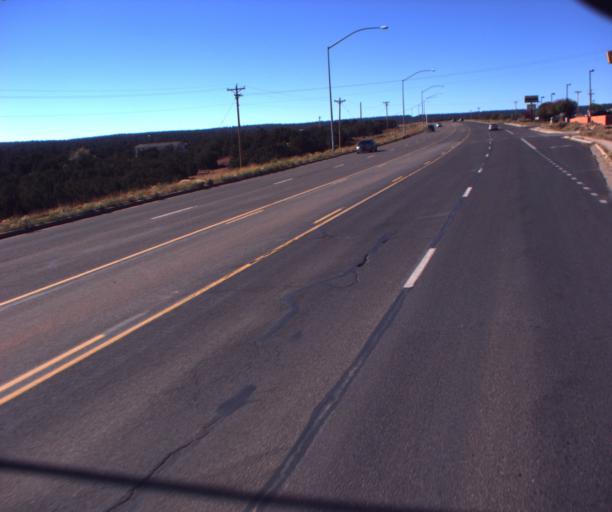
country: US
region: Arizona
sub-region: Apache County
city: Saint Michaels
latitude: 35.6579
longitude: -109.1121
